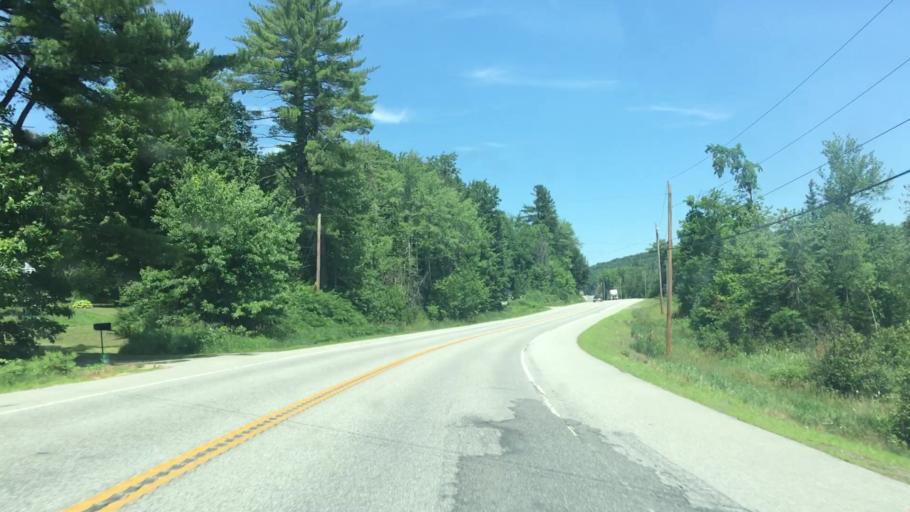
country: US
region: Maine
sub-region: Androscoggin County
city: Livermore
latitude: 44.3982
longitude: -70.2290
